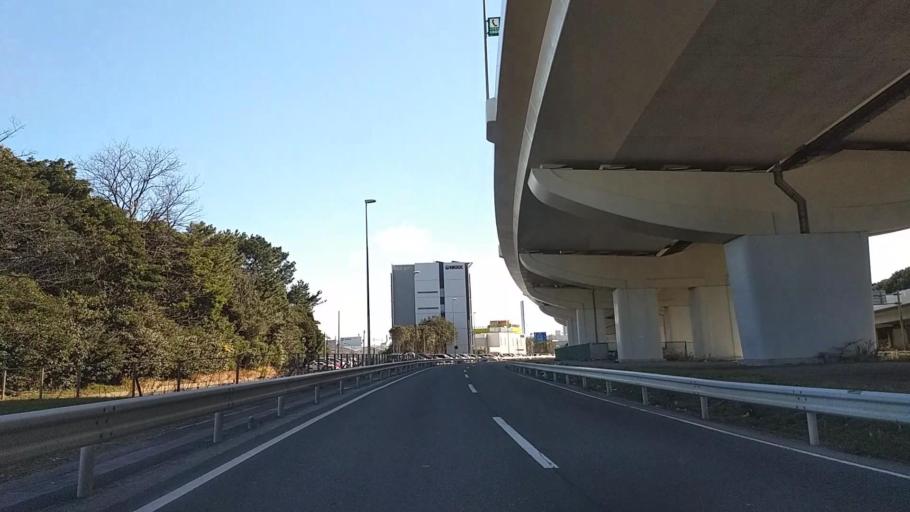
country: JP
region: Kanagawa
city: Yokohama
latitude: 35.3772
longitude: 139.6423
